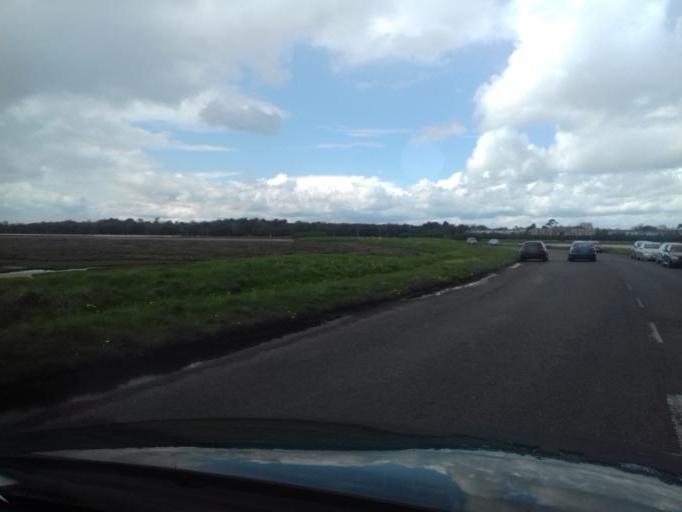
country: IE
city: Bayside
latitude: 53.3713
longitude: -6.1513
